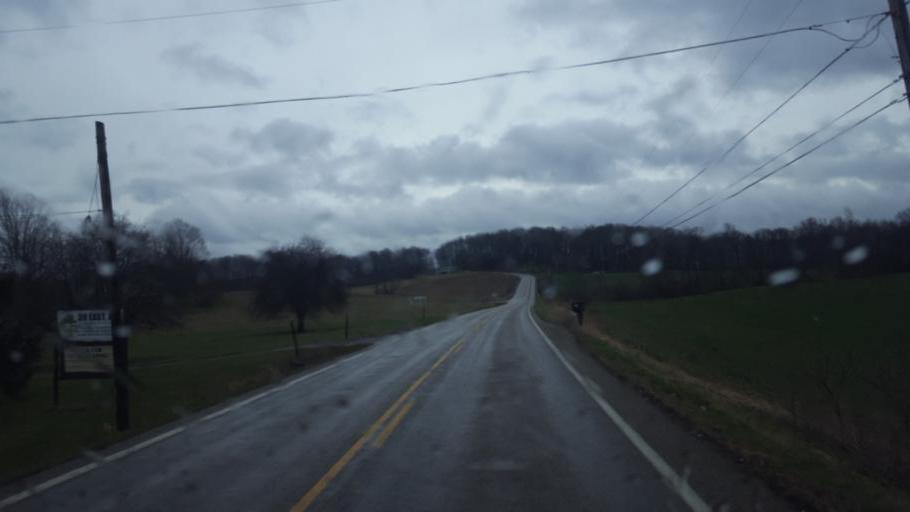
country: US
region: Ohio
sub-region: Ashland County
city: Loudonville
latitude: 40.6342
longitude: -82.2135
